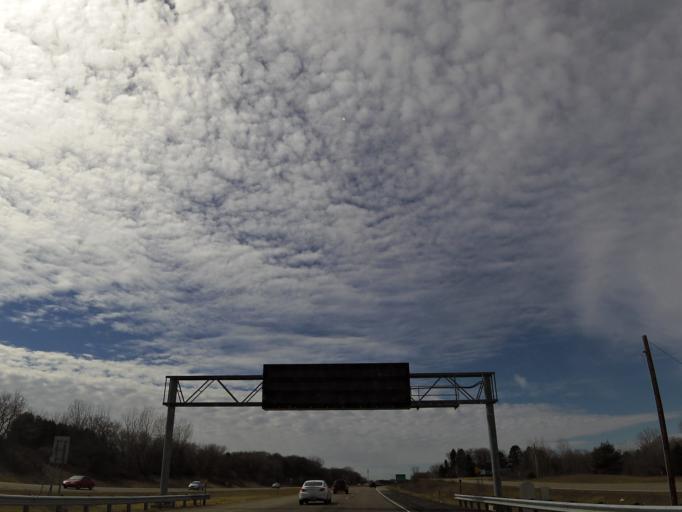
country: US
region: Minnesota
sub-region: Washington County
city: Mahtomedi
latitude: 45.0358
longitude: -92.9344
